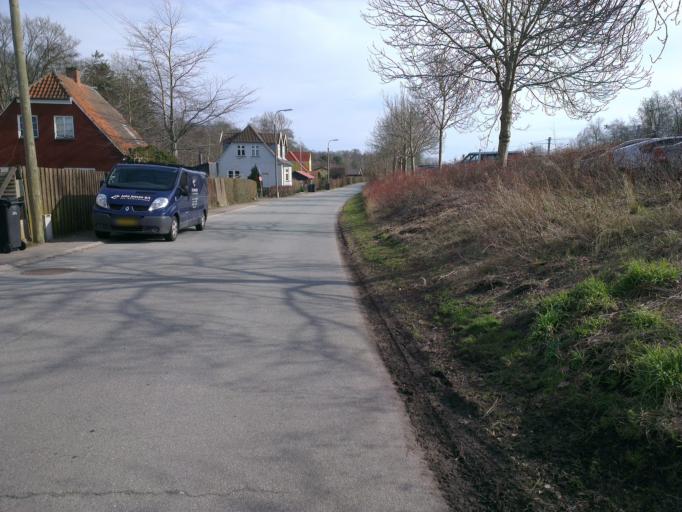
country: DK
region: Capital Region
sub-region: Egedal Kommune
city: Olstykke
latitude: 55.7958
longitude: 12.1603
